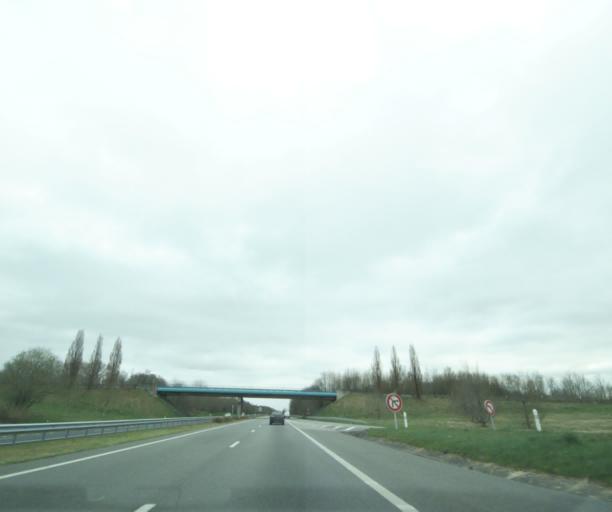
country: FR
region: Limousin
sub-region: Departement de la Correze
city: Uzerche
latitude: 45.3946
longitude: 1.5689
